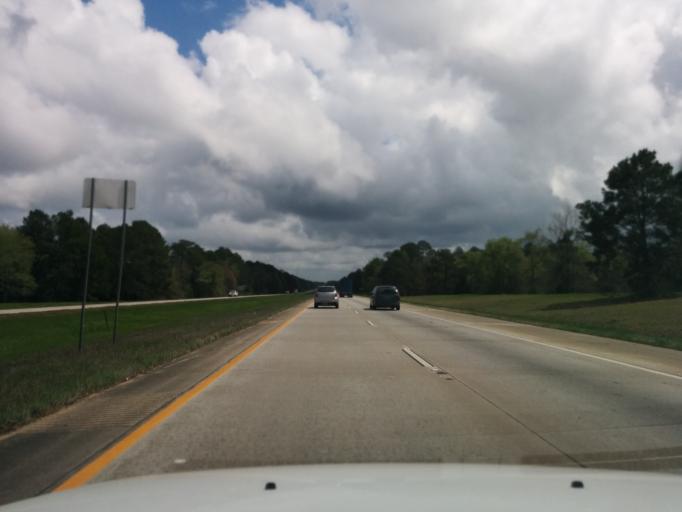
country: US
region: Georgia
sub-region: Evans County
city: Claxton
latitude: 32.3052
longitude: -81.8593
